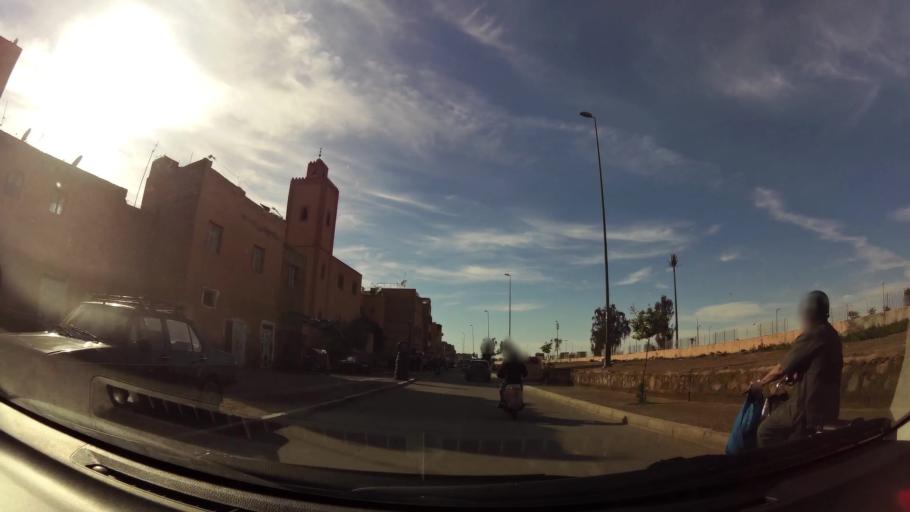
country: MA
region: Marrakech-Tensift-Al Haouz
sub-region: Marrakech
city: Marrakesh
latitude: 31.6202
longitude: -7.9670
